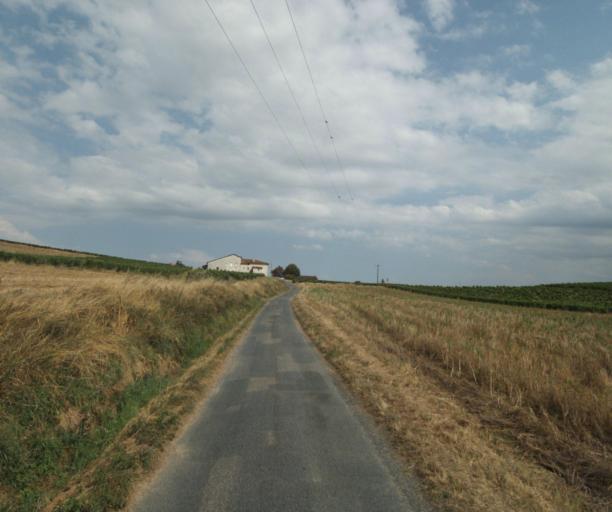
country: FR
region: Rhone-Alpes
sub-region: Departement du Rhone
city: Bully
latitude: 45.8505
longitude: 4.5745
